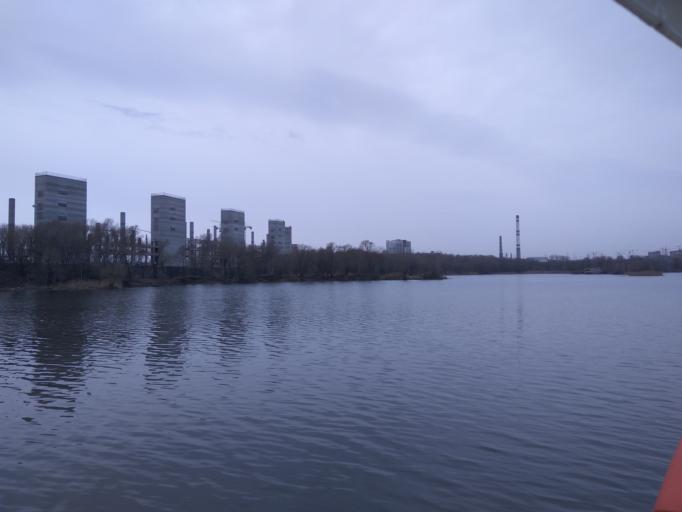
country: RU
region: Moskovskaya
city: Kozhukhovo
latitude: 55.6978
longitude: 37.6828
